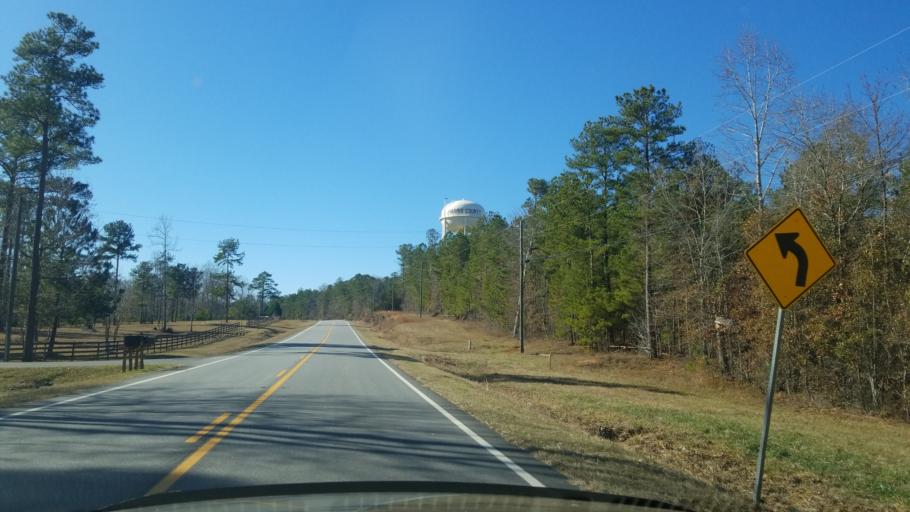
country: US
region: Georgia
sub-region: Harris County
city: Hamilton
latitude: 32.6317
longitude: -84.7602
